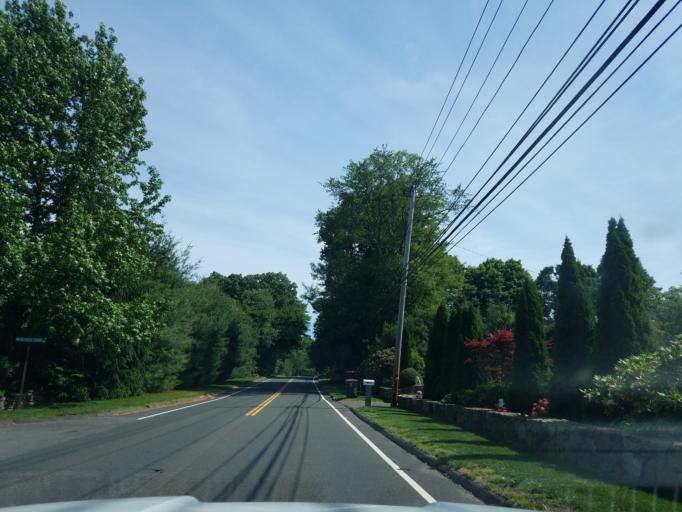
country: US
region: Connecticut
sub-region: Fairfield County
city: Trumbull
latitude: 41.2667
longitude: -73.1660
